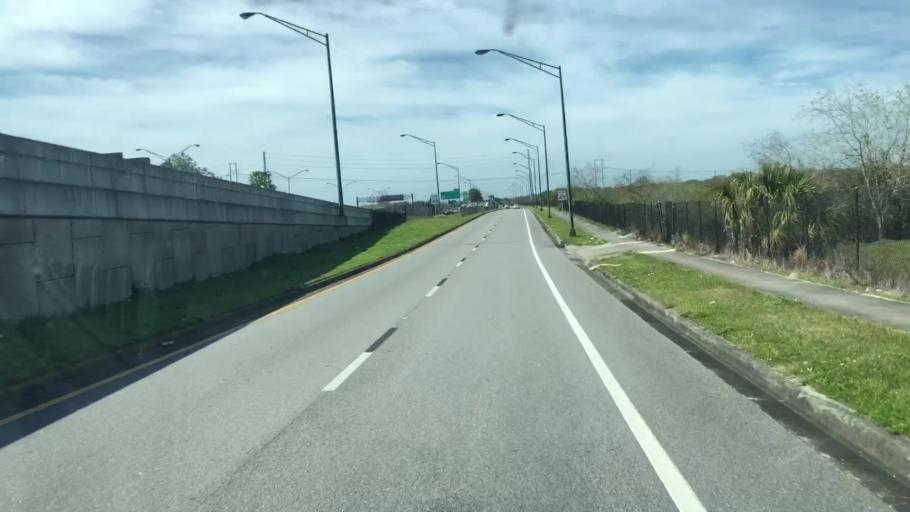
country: US
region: Florida
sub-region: Polk County
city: Medulla
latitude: 27.9973
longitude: -81.9850
